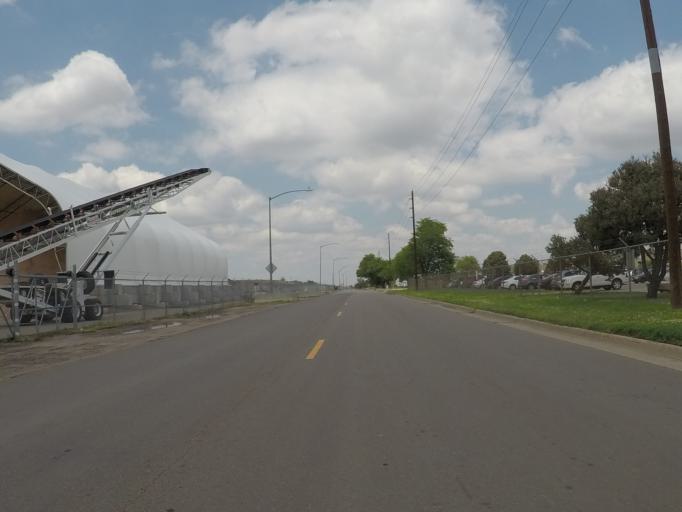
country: US
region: Colorado
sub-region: Adams County
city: Commerce City
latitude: 39.7948
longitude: -104.9015
